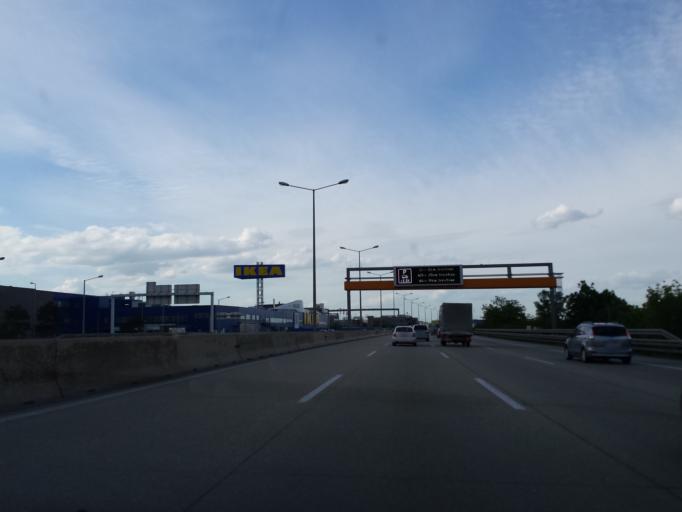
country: AT
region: Lower Austria
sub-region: Politischer Bezirk Modling
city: Wiener Neudorf
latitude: 48.1036
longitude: 16.3206
